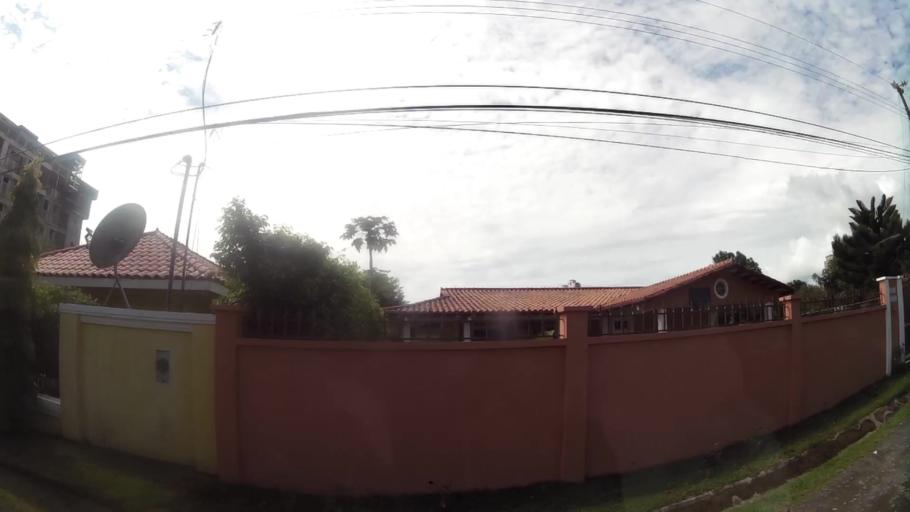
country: PA
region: Panama
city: Nueva Gorgona
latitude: 8.5432
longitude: -79.8812
